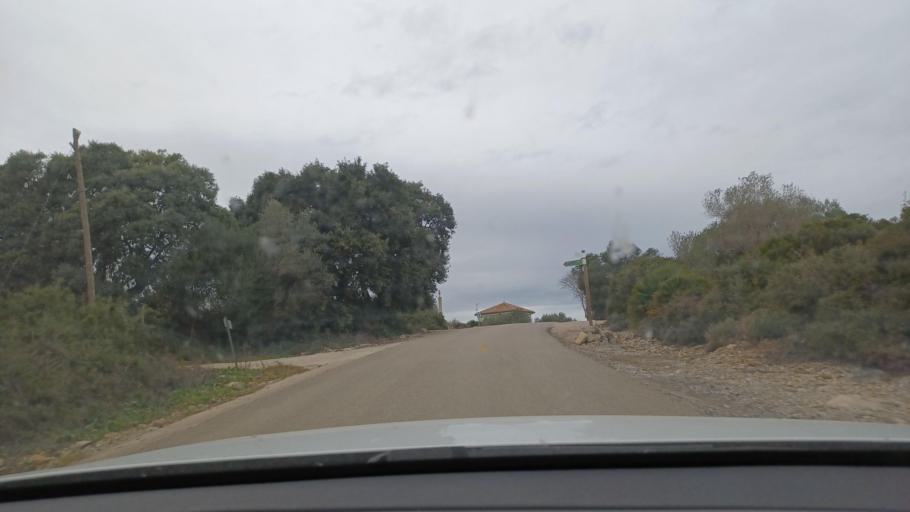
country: ES
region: Valencia
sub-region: Provincia de Castello
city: Traiguera
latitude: 40.5051
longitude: 0.2956
